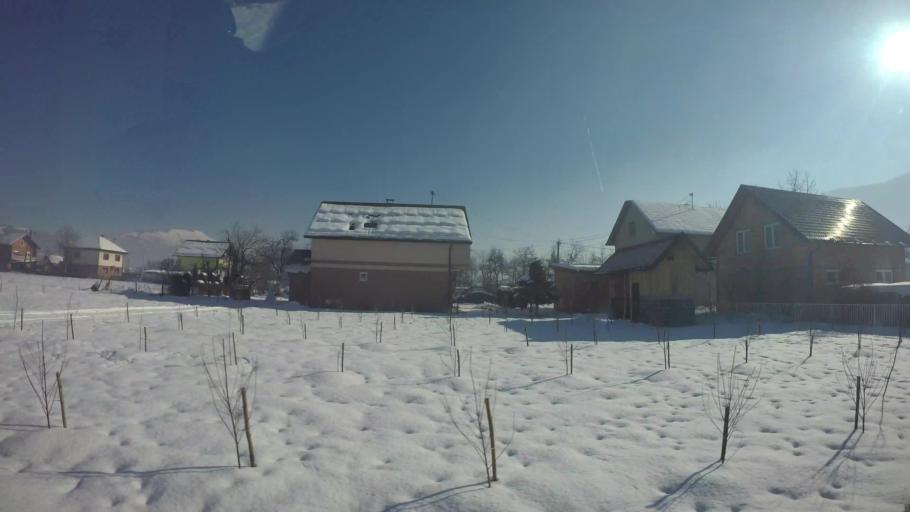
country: BA
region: Federation of Bosnia and Herzegovina
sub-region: Kanton Sarajevo
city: Sarajevo
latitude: 43.7929
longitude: 18.3399
